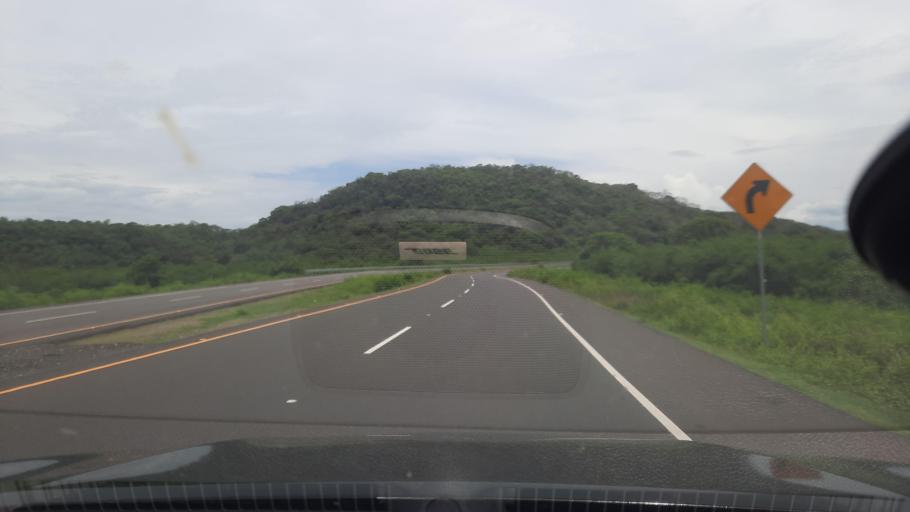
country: HN
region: Valle
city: Aramecina
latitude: 13.7281
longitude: -87.7141
